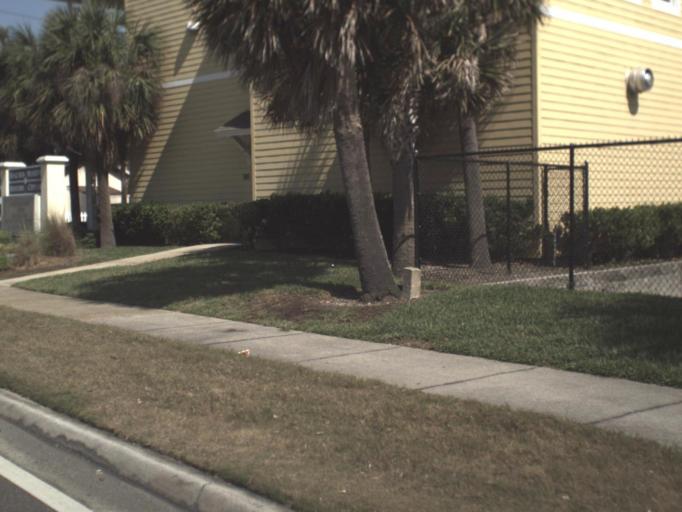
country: US
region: Florida
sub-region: Duval County
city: Jacksonville Beach
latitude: 30.2884
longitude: -81.3926
